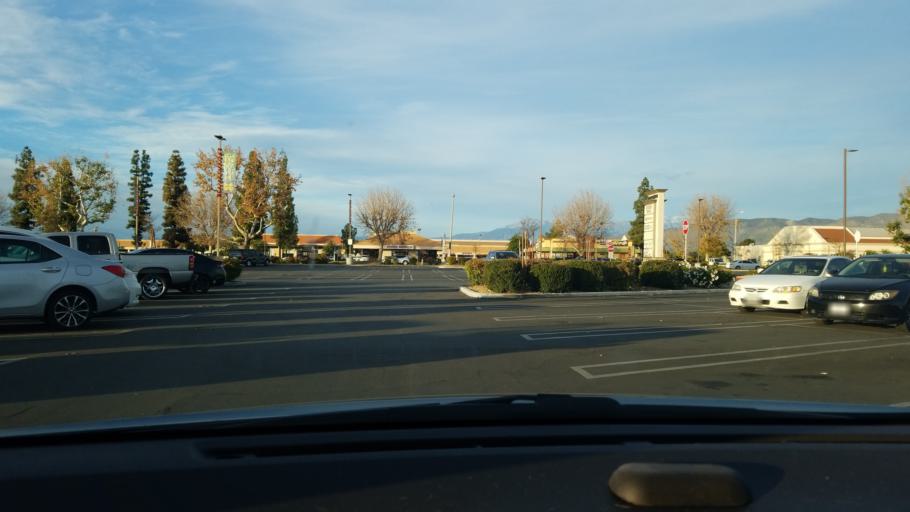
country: US
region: California
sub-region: Riverside County
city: Hemet
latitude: 33.7464
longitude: -117.0051
